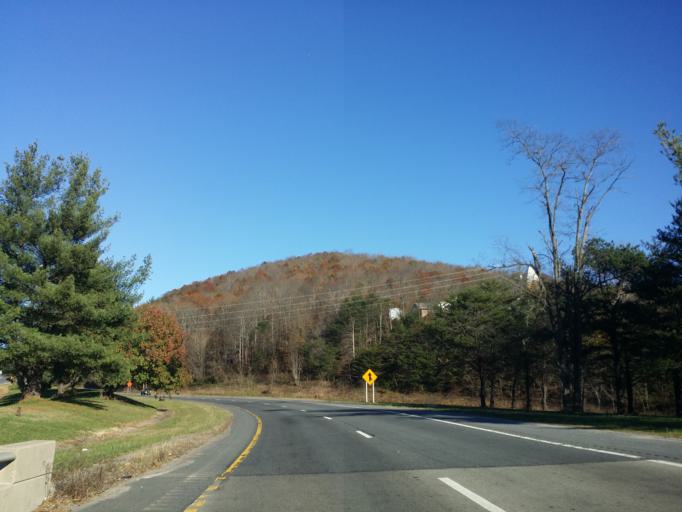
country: US
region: North Carolina
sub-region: Buncombe County
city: Biltmore Forest
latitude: 35.5667
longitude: -82.4970
